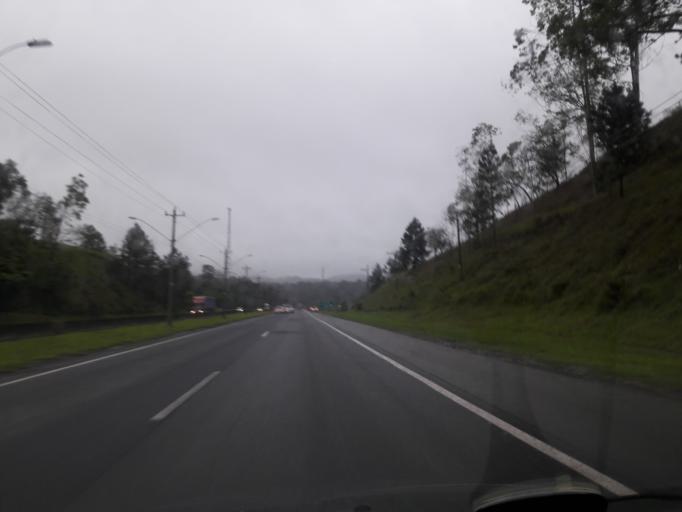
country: BR
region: Sao Paulo
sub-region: Sao Lourenco Da Serra
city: Sao Lourenco da Serra
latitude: -23.8636
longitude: -46.9481
